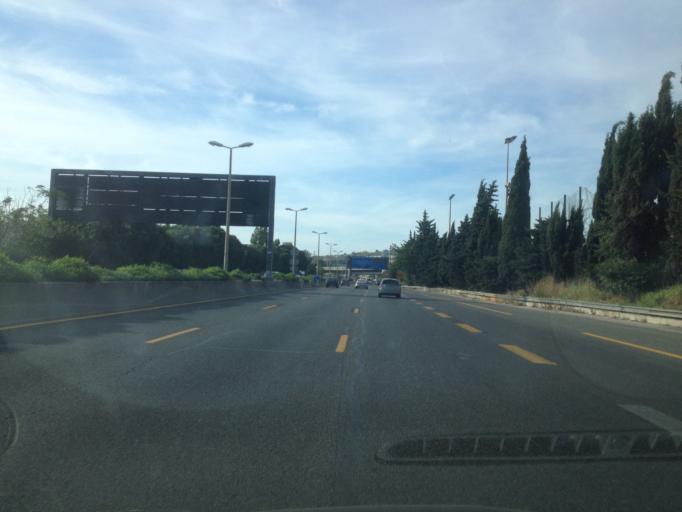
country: FR
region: Provence-Alpes-Cote d'Azur
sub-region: Departement des Bouches-du-Rhone
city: Marseille 14
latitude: 43.3354
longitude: 5.3773
